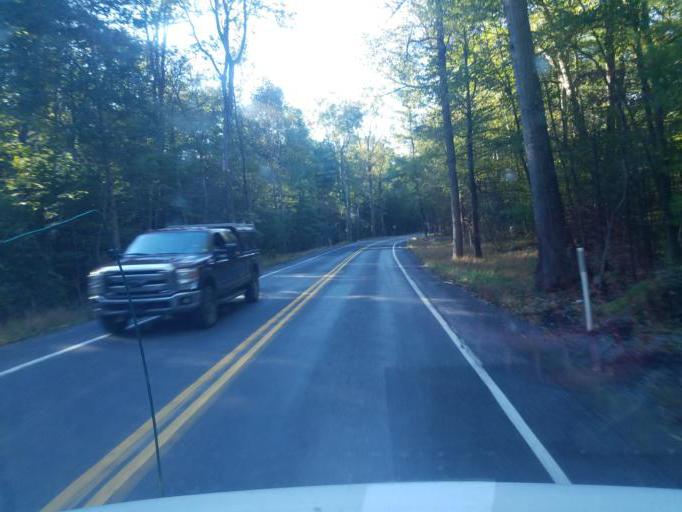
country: US
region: Pennsylvania
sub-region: Franklin County
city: Mont Alto
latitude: 39.8537
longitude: -77.5034
